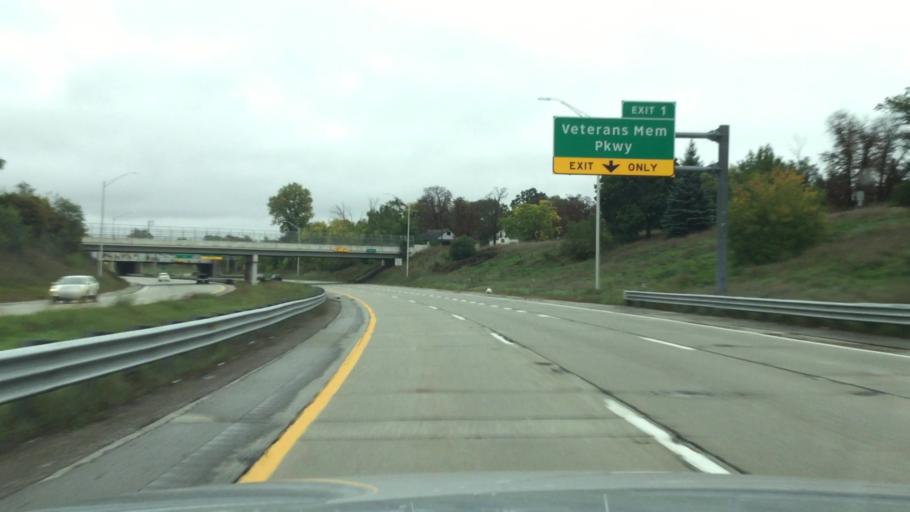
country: US
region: Michigan
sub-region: Saginaw County
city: Buena Vista
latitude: 43.4345
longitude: -83.9195
